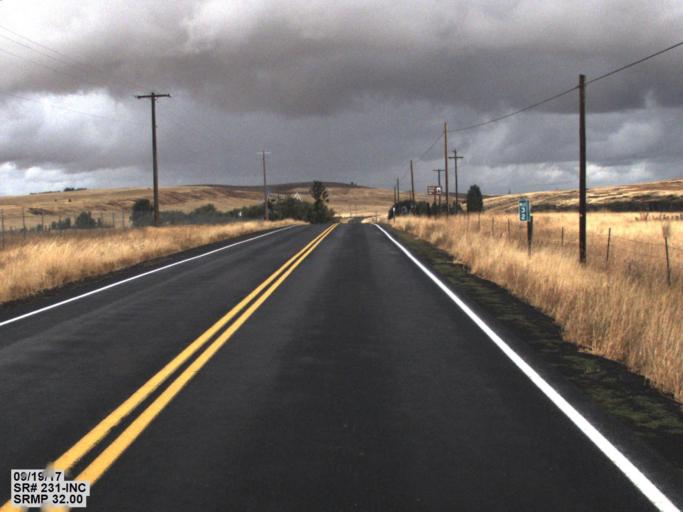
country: US
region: Washington
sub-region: Spokane County
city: Medical Lake
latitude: 47.6826
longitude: -117.8800
